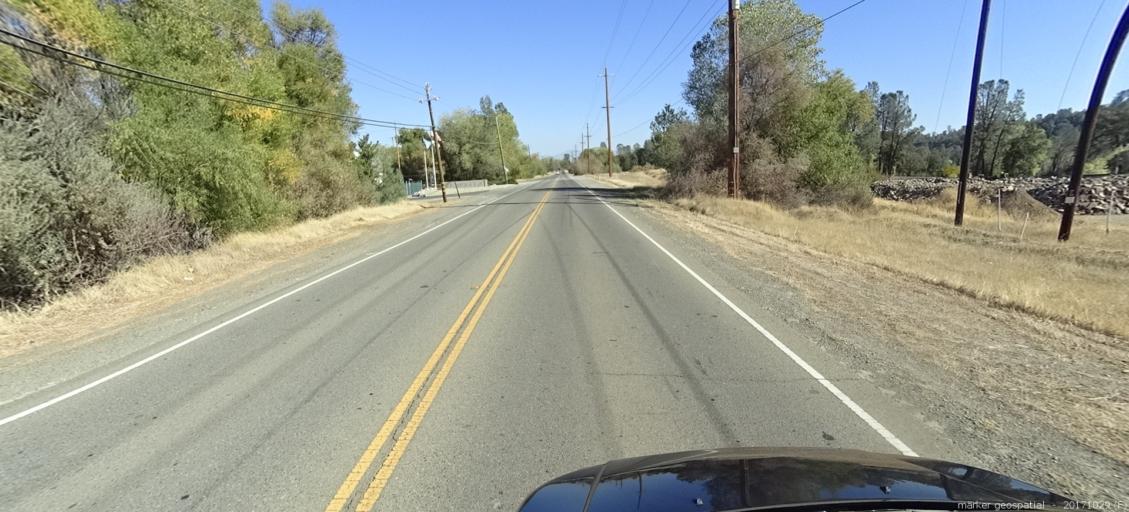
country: US
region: California
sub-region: Shasta County
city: Redding
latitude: 40.5045
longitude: -122.4154
